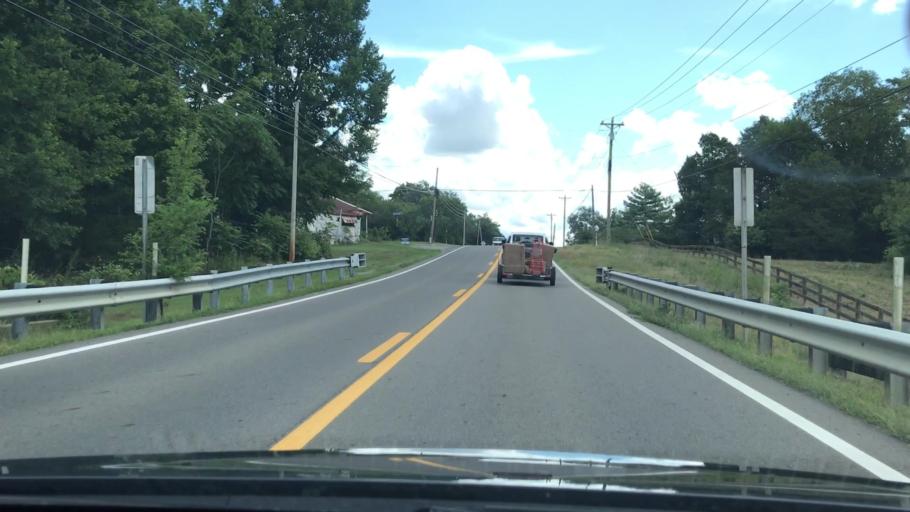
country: US
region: Tennessee
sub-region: Rutherford County
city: Smyrna
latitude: 35.8472
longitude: -86.5621
